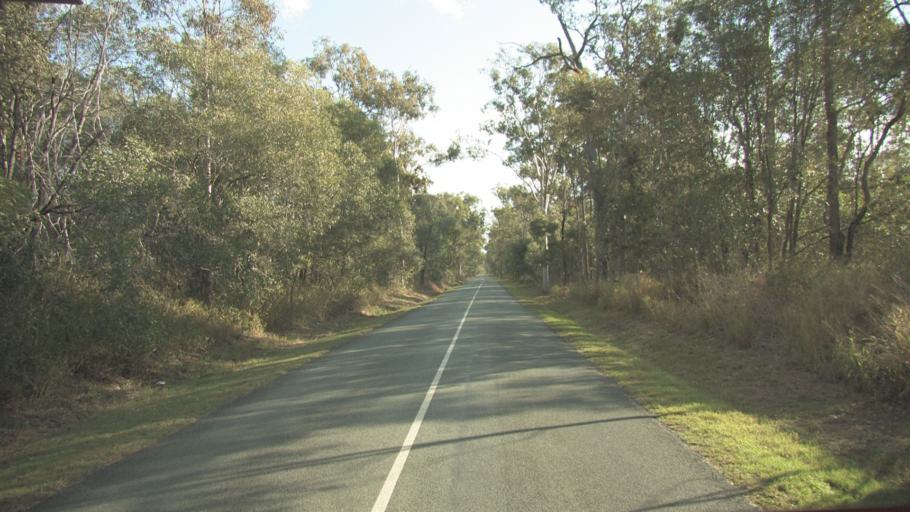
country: AU
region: Queensland
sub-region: Logan
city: Cedar Vale
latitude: -27.8506
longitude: 153.1333
